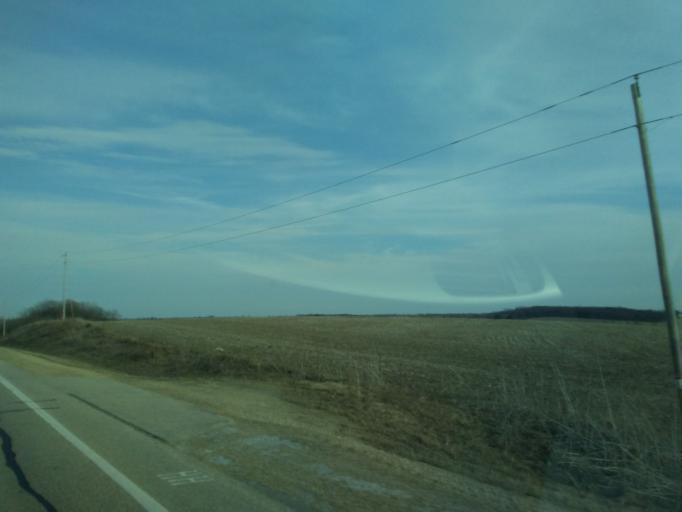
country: US
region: Wisconsin
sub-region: Grant County
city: Fennimore
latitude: 42.9735
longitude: -90.5078
